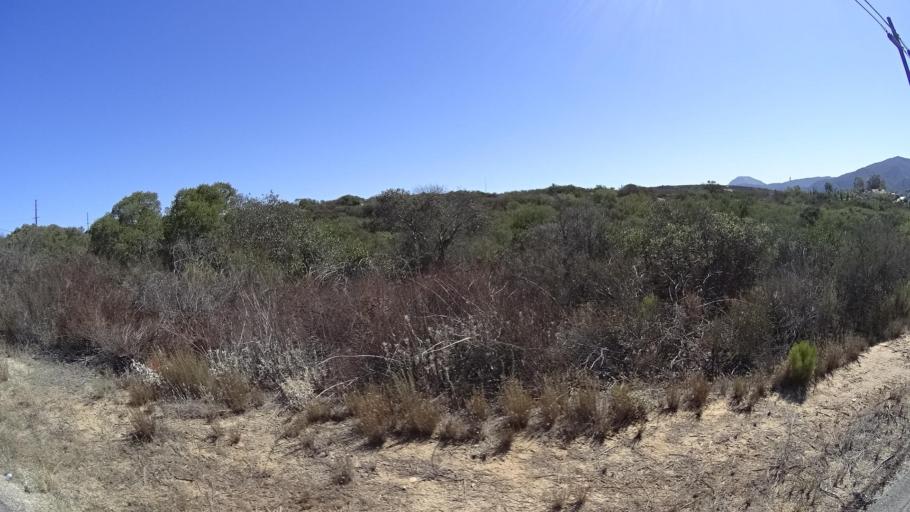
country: US
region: California
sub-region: San Diego County
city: Harbison Canyon
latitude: 32.7948
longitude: -116.8026
